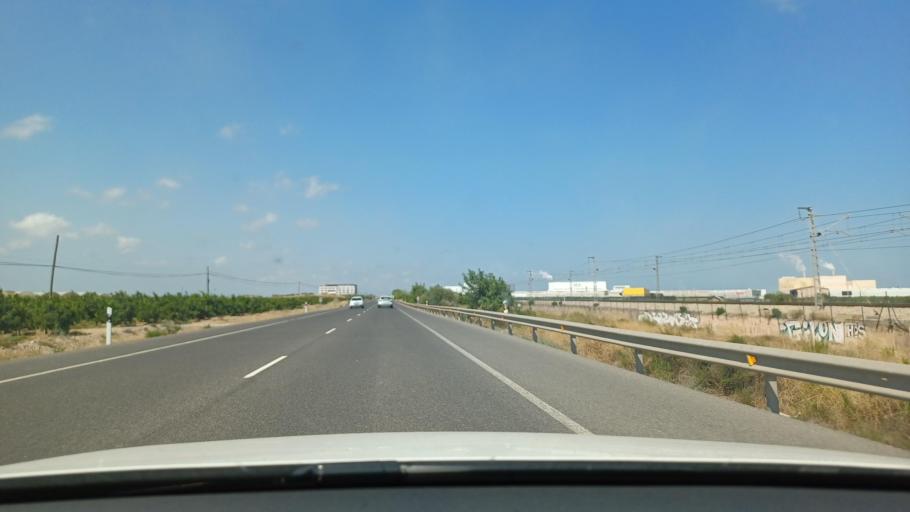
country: ES
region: Valencia
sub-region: Provincia de Castello
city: Chilches
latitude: 39.7874
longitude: -0.1869
